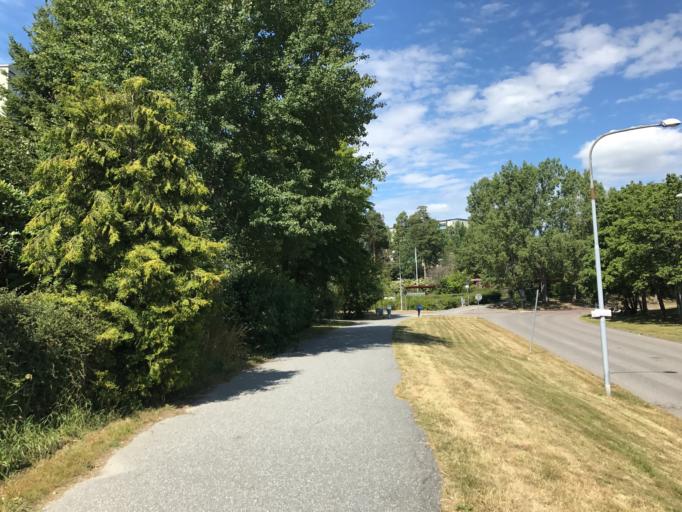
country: SE
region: Stockholm
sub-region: Stockholms Kommun
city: Kista
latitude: 59.4033
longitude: 17.9325
